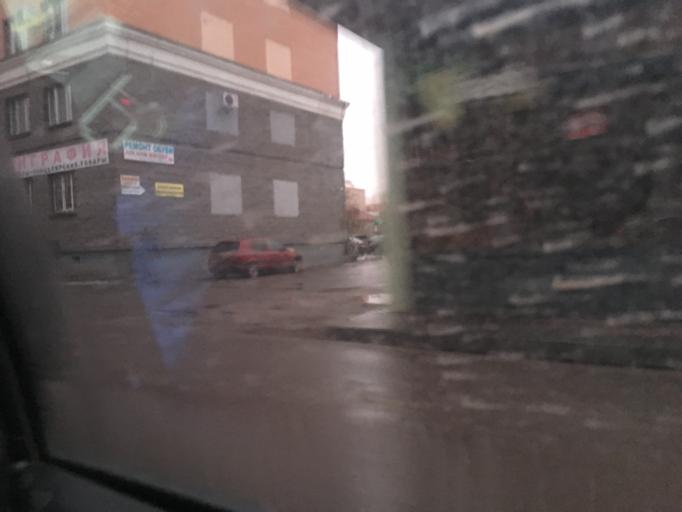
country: KZ
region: Astana Qalasy
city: Astana
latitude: 51.1589
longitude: 71.4362
